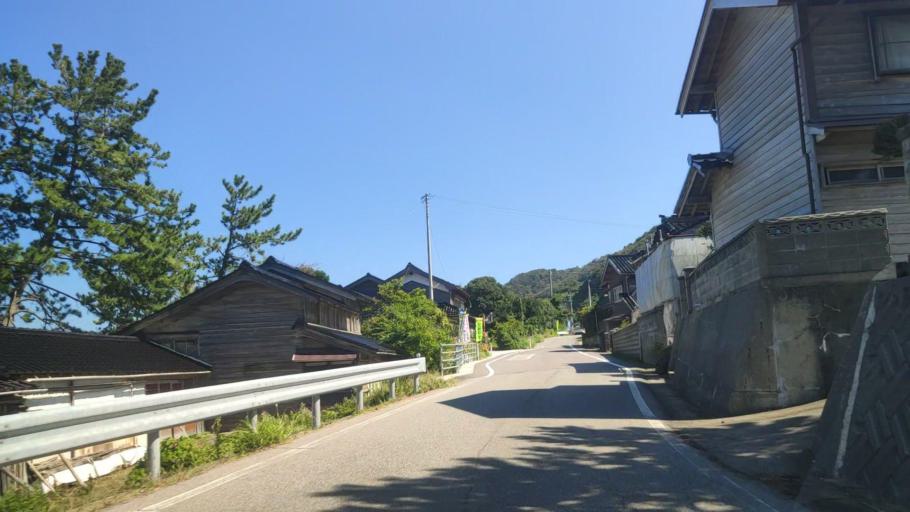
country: JP
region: Ishikawa
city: Nanao
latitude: 37.5059
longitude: 137.2060
